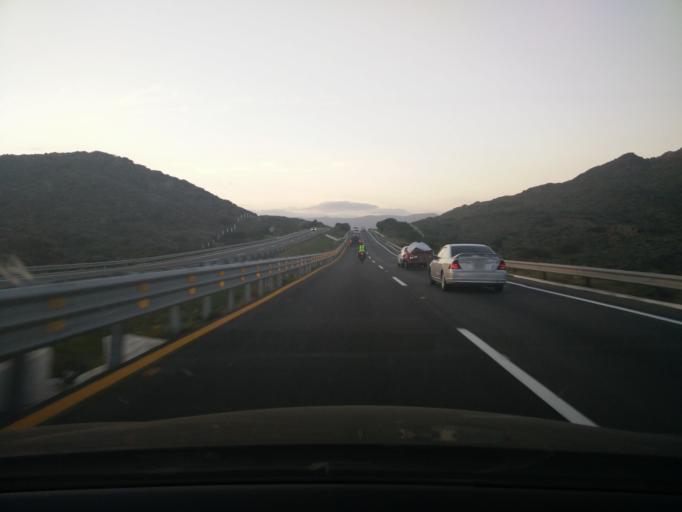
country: MX
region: Baja California
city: El Sauzal
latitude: 31.9088
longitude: -116.7504
